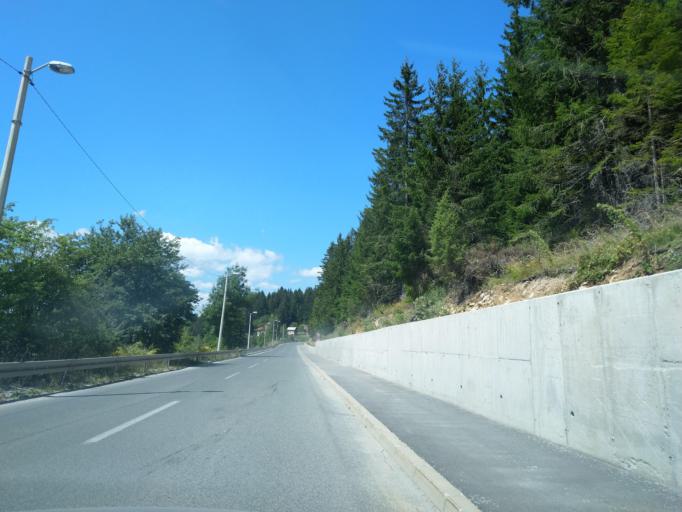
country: RS
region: Central Serbia
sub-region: Zlatiborski Okrug
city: Nova Varos
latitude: 43.4403
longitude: 19.8213
